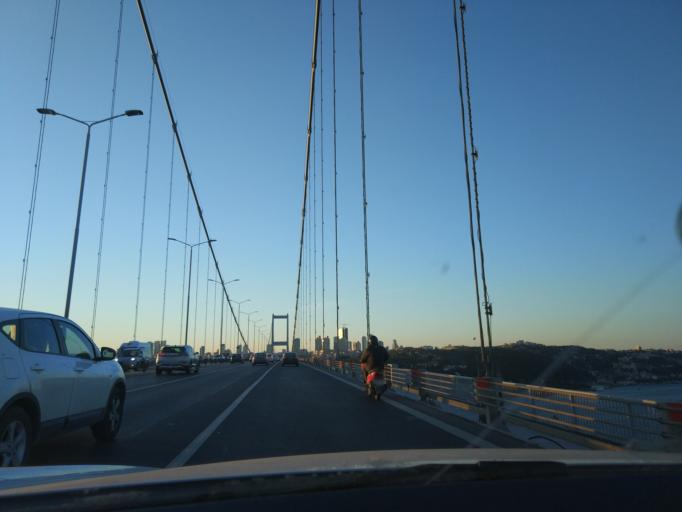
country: TR
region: Istanbul
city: UEskuedar
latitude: 41.0424
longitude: 29.0378
